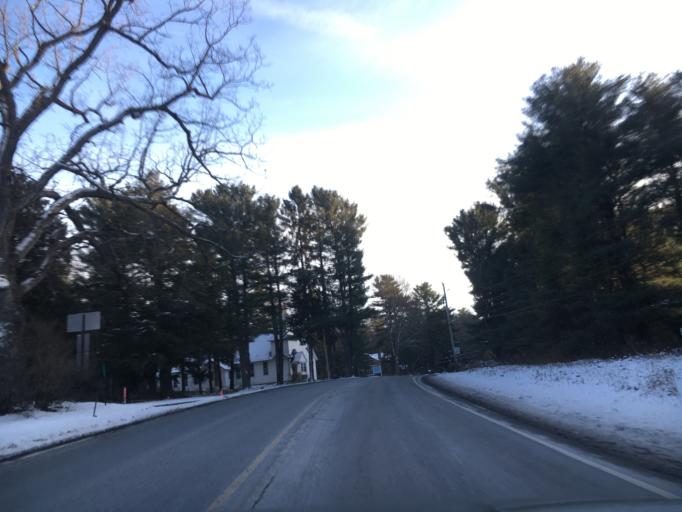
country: US
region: Pennsylvania
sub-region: Pike County
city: Hemlock Farms
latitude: 41.3721
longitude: -75.1276
